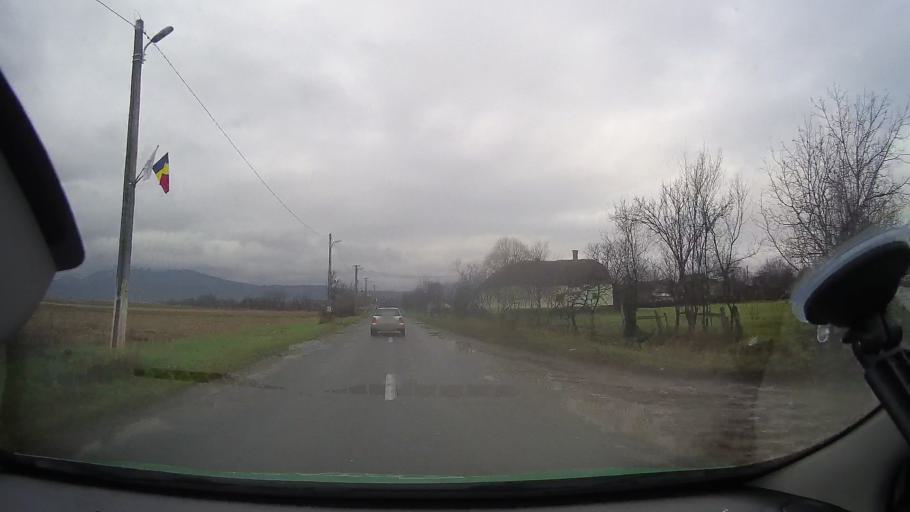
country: RO
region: Arad
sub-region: Comuna Buteni
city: Buteni
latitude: 46.3347
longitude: 22.1265
